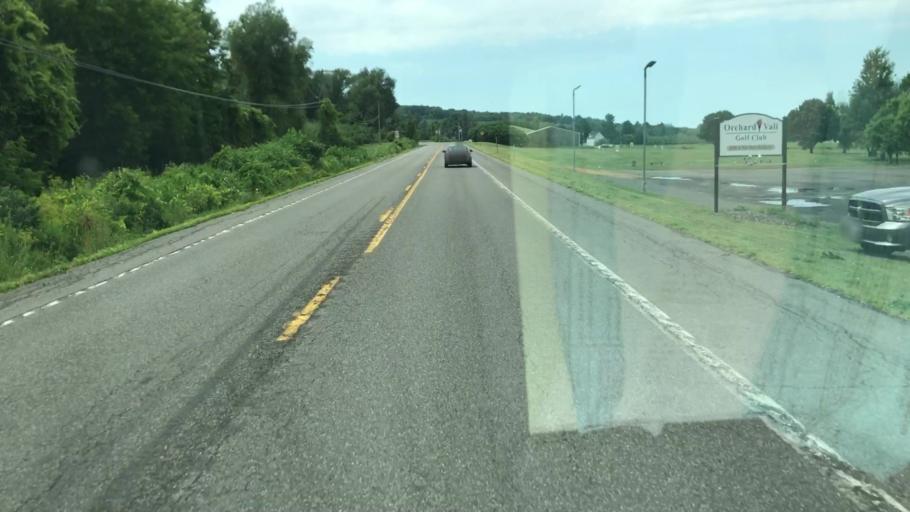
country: US
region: New York
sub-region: Onondaga County
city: Nedrow
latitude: 42.9084
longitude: -76.1902
